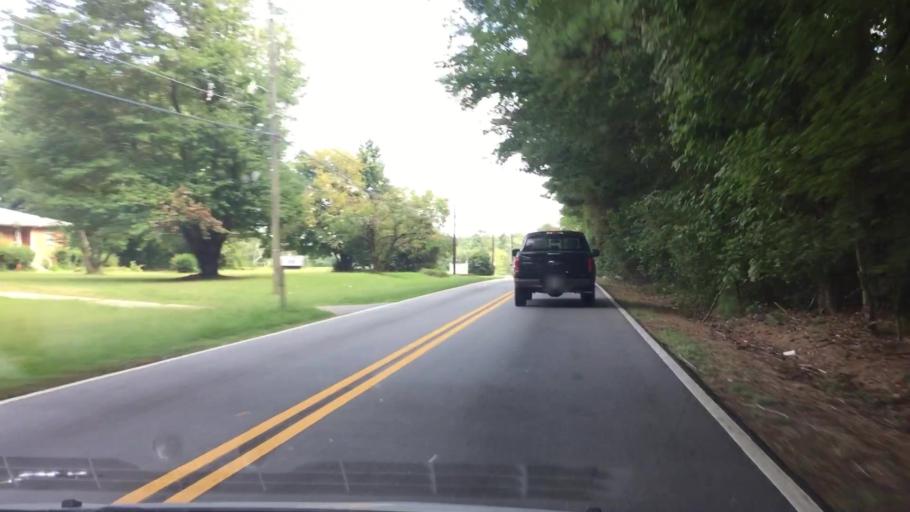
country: US
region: Georgia
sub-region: Clayton County
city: Conley
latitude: 33.6673
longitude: -84.3070
